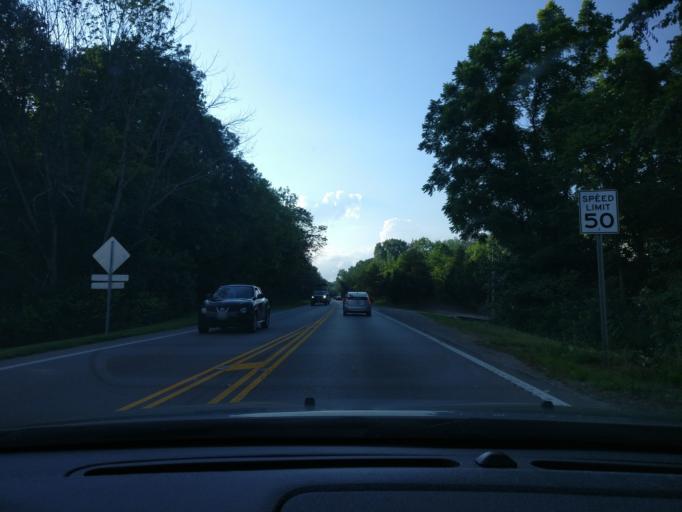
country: US
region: Ohio
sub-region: Warren County
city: Waynesville
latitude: 39.5275
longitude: -84.0906
